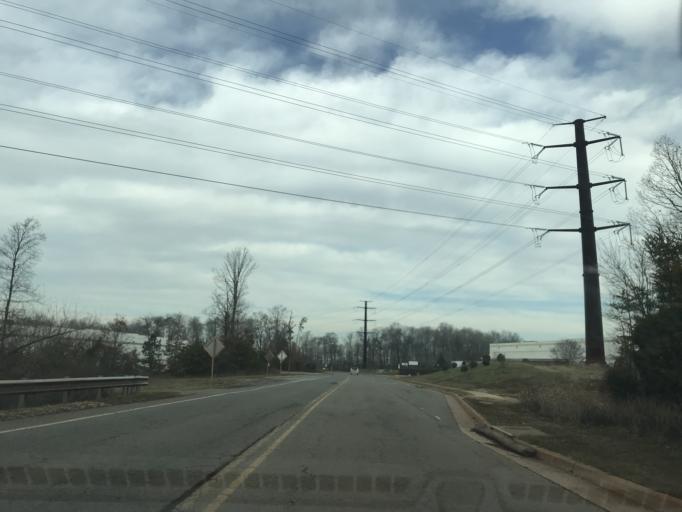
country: US
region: Virginia
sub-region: City of Manassas
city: Manassas
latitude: 38.7237
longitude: -77.5017
